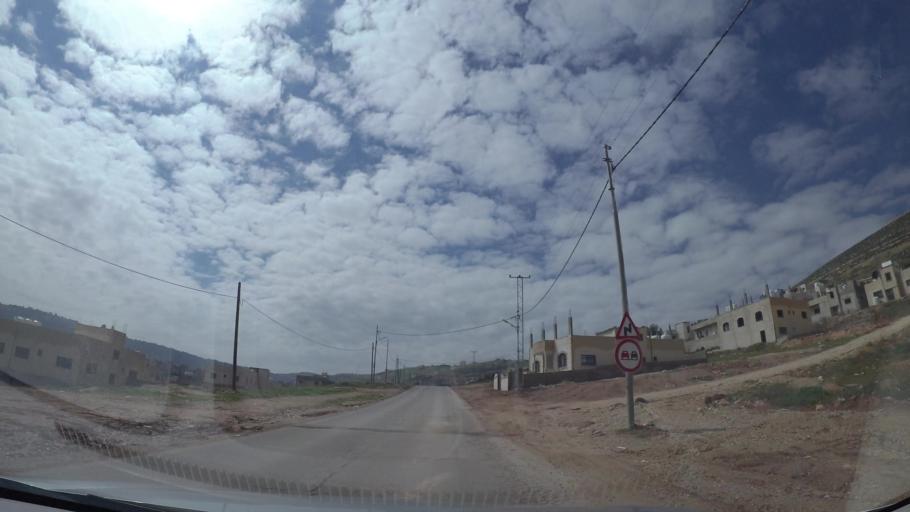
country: JO
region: Amman
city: Al Jubayhah
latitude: 32.0659
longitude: 35.8125
